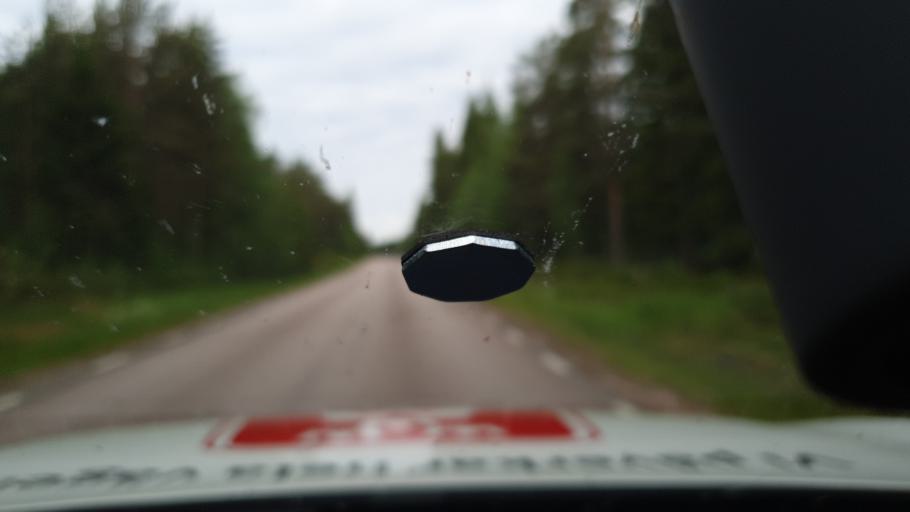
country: SE
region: Vaermland
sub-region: Torsby Kommun
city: Torsby
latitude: 60.1130
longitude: 12.9244
